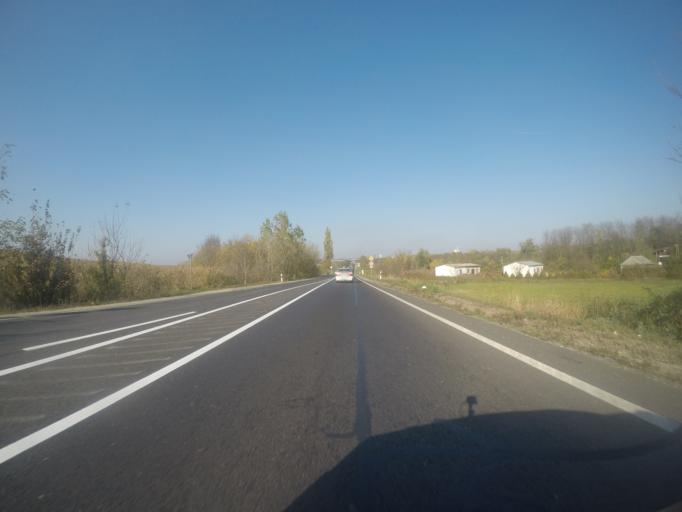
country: HU
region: Fejer
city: Baracs
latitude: 46.9028
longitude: 18.9242
